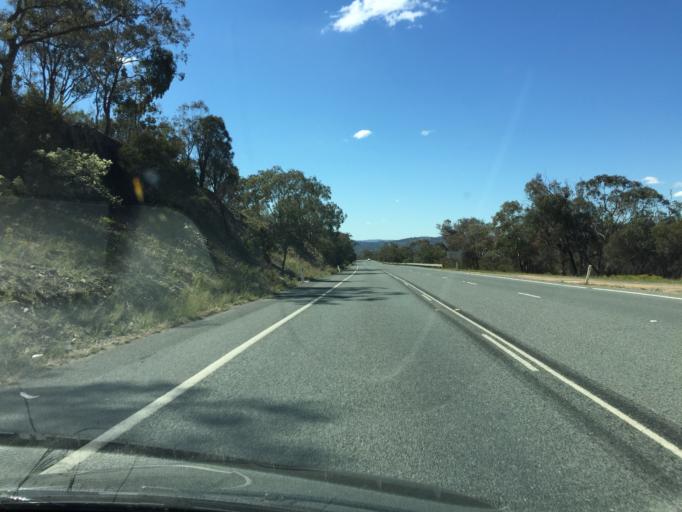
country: AU
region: Australian Capital Territory
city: Macarthur
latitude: -35.4635
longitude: 149.1346
